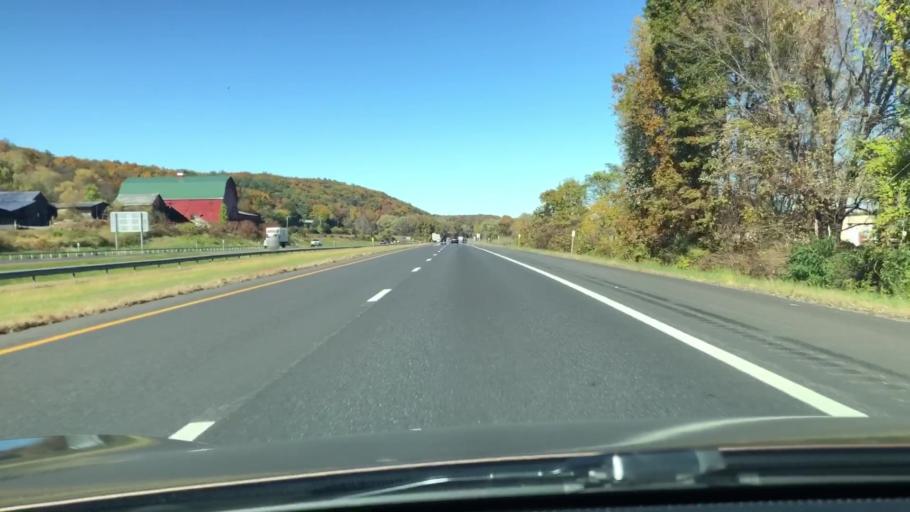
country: US
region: New York
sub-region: Ulster County
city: Lincoln Park
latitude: 41.9597
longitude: -74.0154
